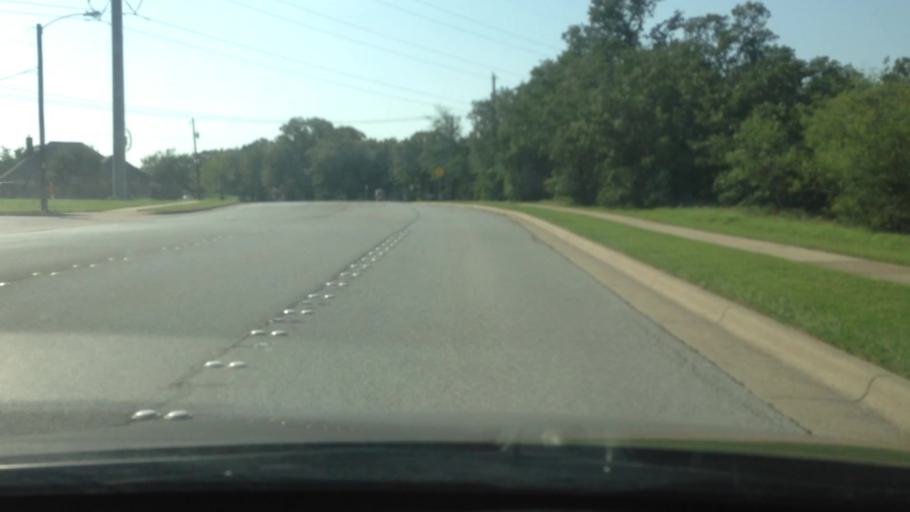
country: US
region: Texas
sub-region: Tarrant County
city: Colleyville
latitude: 32.8836
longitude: -97.1886
